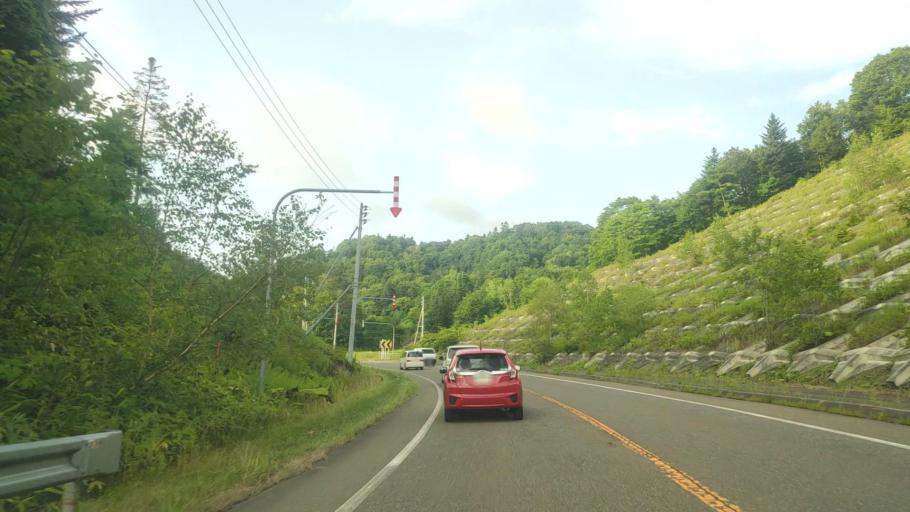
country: JP
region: Hokkaido
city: Iwamizawa
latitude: 43.0232
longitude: 141.9541
